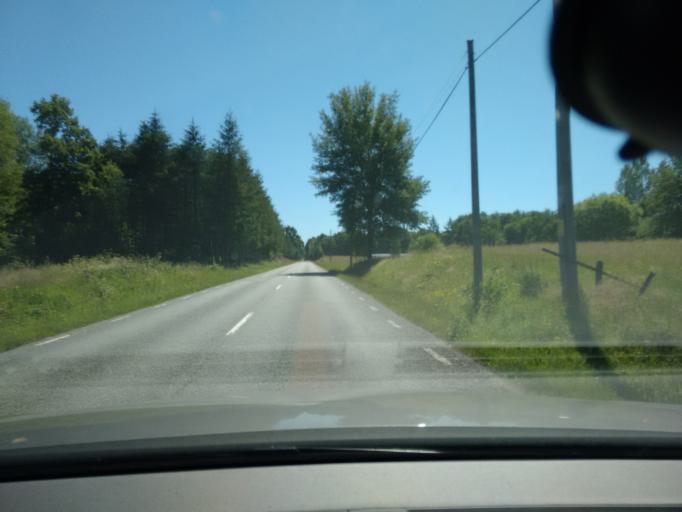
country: SE
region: Skane
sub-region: Kristianstads Kommun
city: Degeberga
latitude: 55.7662
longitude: 13.9066
